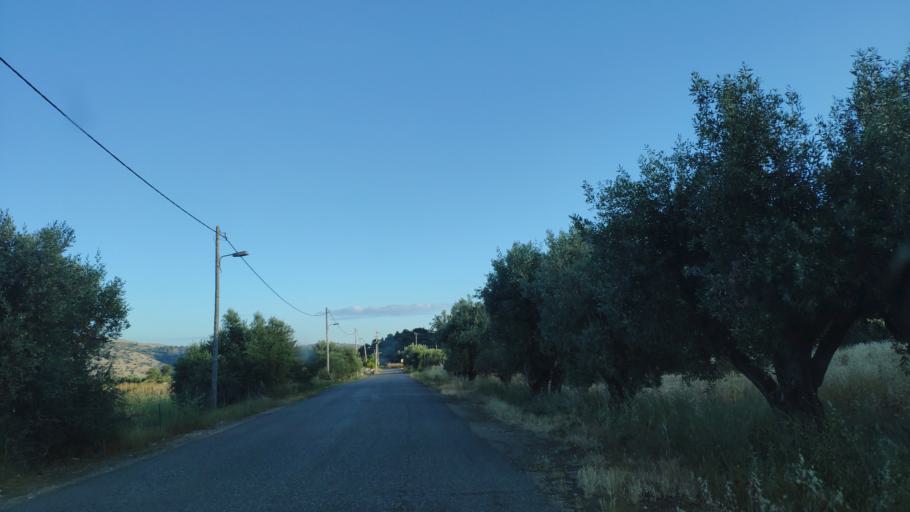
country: GR
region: West Greece
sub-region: Nomos Aitolias kai Akarnanias
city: Astakos
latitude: 38.5689
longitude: 21.0950
